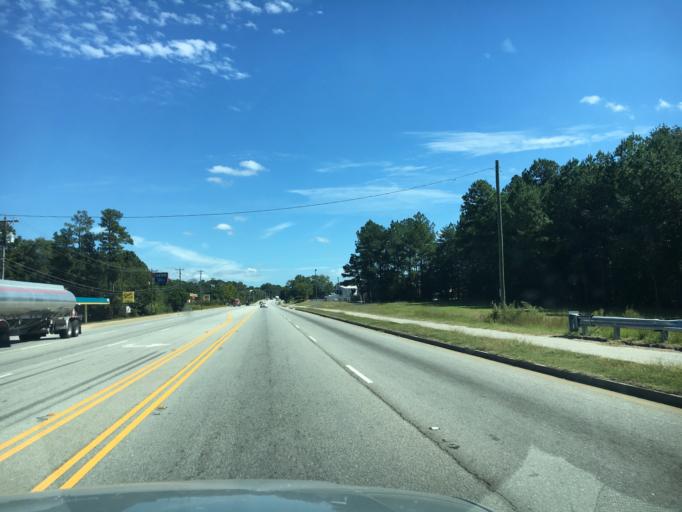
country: US
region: South Carolina
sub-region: Spartanburg County
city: Spartanburg
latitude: 34.9179
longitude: -81.8960
